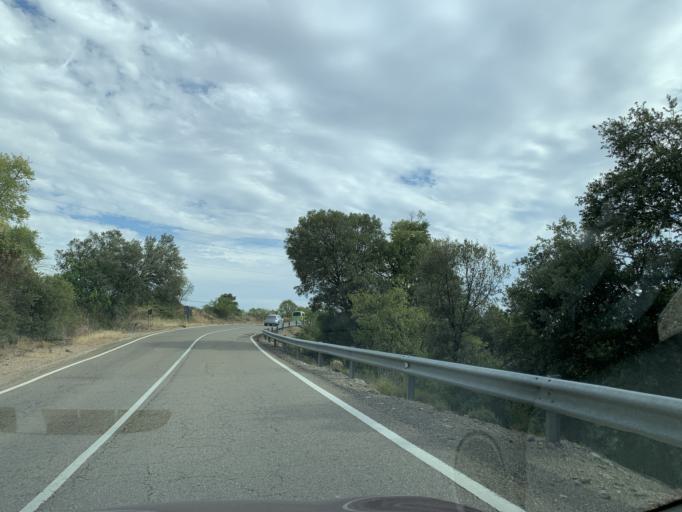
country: ES
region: Aragon
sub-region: Provincia de Zaragoza
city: Santa Eulalia de Gallego
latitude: 42.3150
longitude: -0.7532
